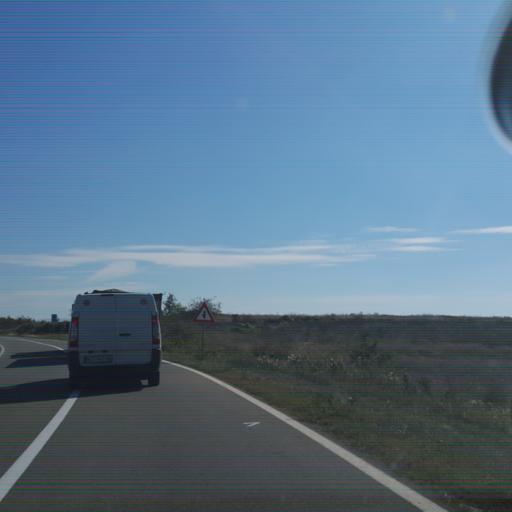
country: RS
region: Central Serbia
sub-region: Zajecarski Okrug
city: Knjazevac
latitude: 43.4869
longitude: 22.2265
